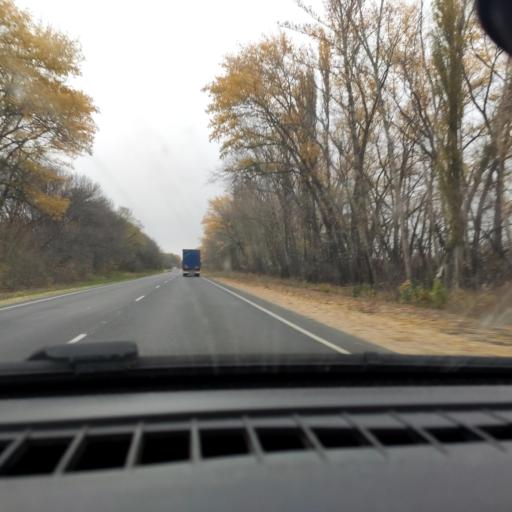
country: RU
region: Voronezj
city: Uryv-Pokrovka
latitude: 51.1770
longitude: 39.0792
